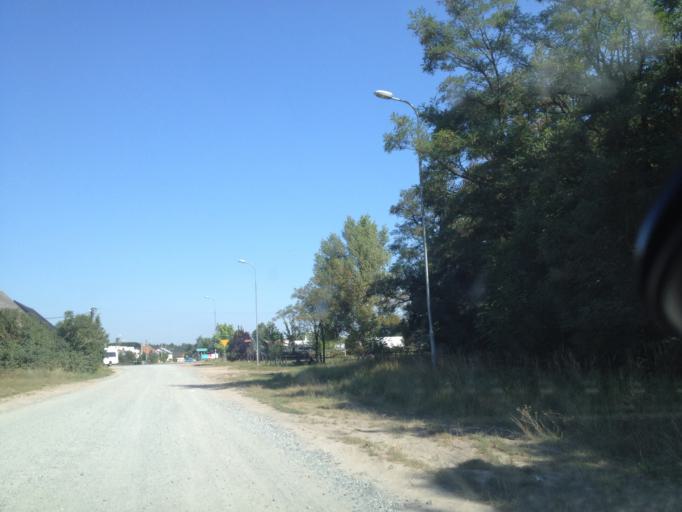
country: PL
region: Greater Poland Voivodeship
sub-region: Powiat sredzki
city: Zaniemysl
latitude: 52.1118
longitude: 17.1181
